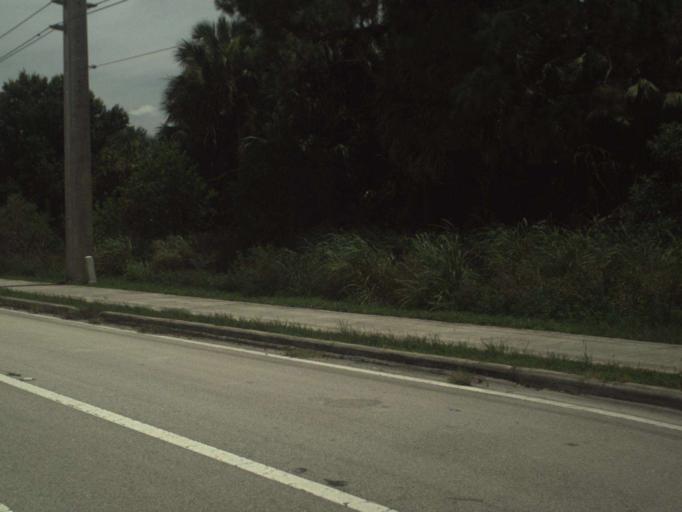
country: US
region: Florida
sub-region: Saint Lucie County
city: Lakewood Park
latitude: 27.5281
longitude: -80.4147
